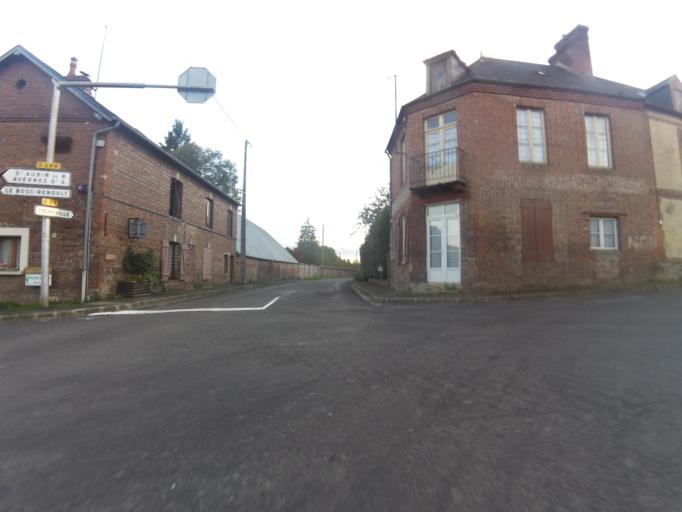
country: FR
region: Lower Normandy
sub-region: Departement de l'Orne
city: Vimoutiers
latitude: 48.9284
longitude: 0.2661
